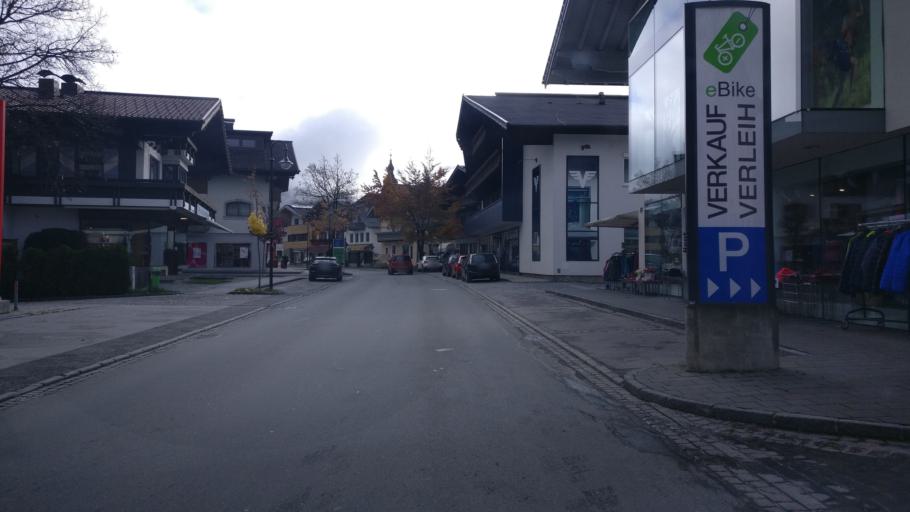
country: AT
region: Salzburg
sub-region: Politischer Bezirk Sankt Johann im Pongau
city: Altenmarkt im Pongau
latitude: 47.3796
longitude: 13.4202
